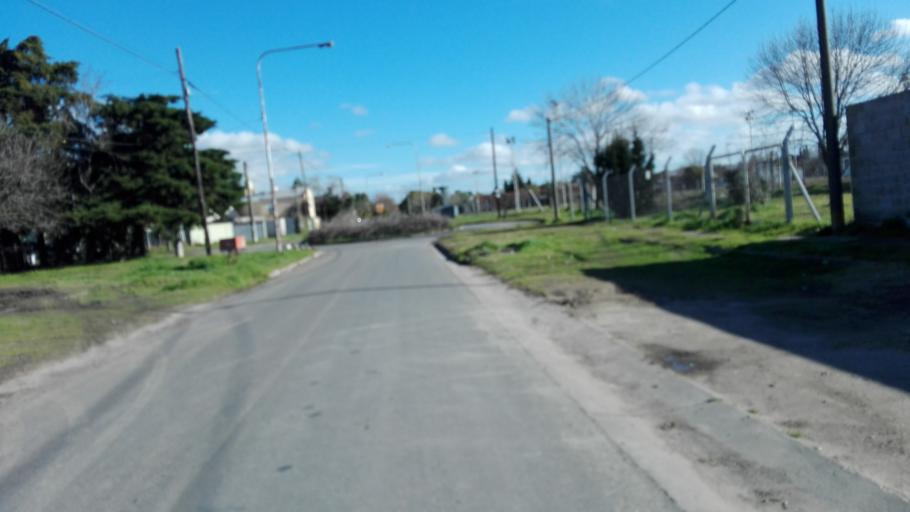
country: AR
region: Buenos Aires
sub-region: Partido de La Plata
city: La Plata
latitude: -34.8800
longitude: -57.9979
